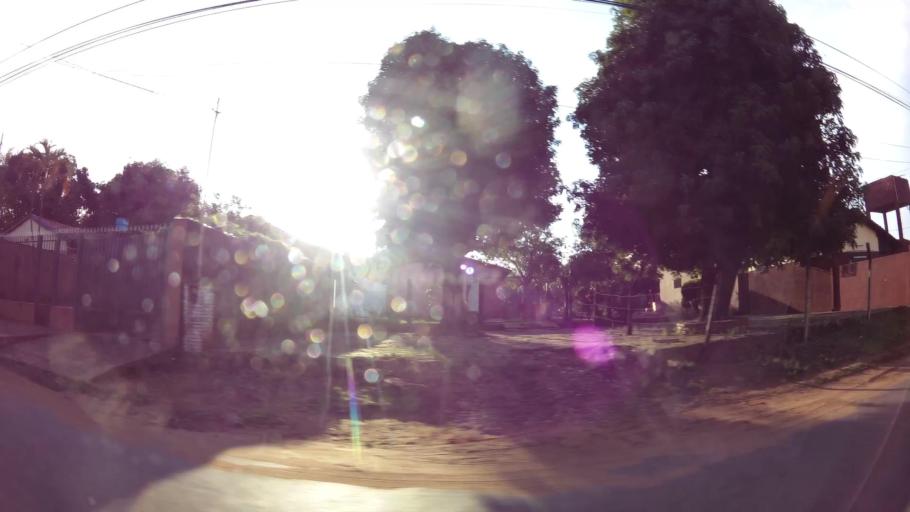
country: PY
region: Central
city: Fernando de la Mora
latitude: -25.3604
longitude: -57.5295
